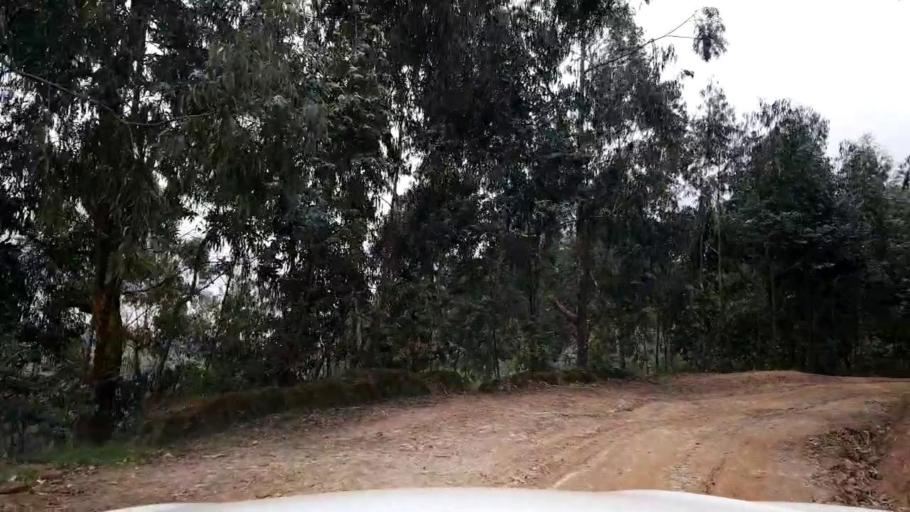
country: RW
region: Western Province
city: Kibuye
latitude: -1.9372
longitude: 29.4479
